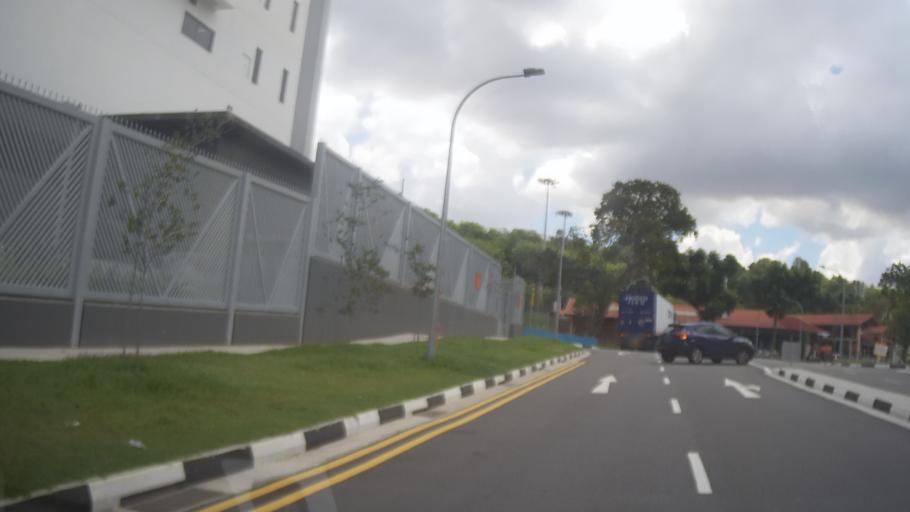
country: MY
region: Johor
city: Johor Bahru
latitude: 1.4334
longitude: 103.7793
